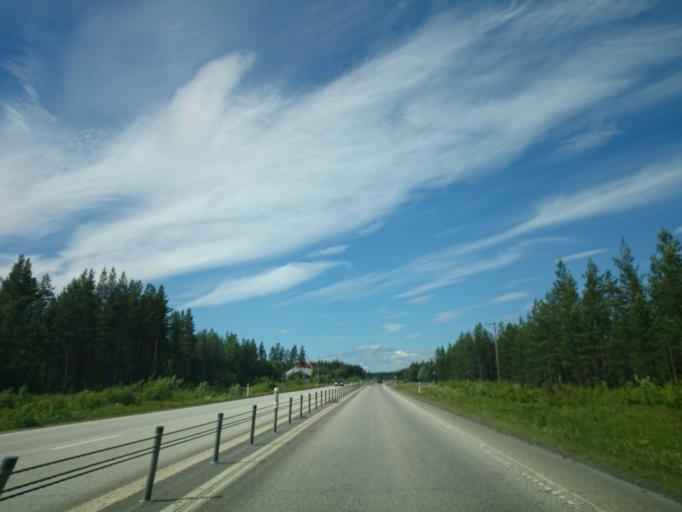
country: SE
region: Jaemtland
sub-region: OEstersunds Kommun
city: Ostersund
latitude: 63.2356
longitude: 14.6073
